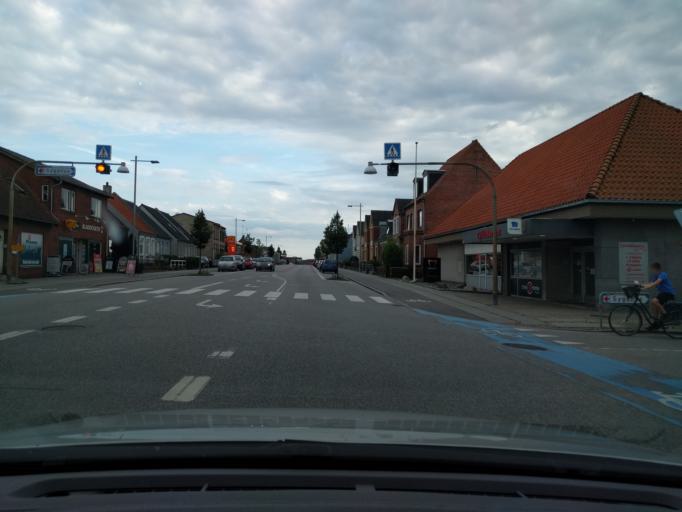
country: DK
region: Zealand
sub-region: Guldborgsund Kommune
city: Nykobing Falster
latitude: 54.7786
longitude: 11.8669
